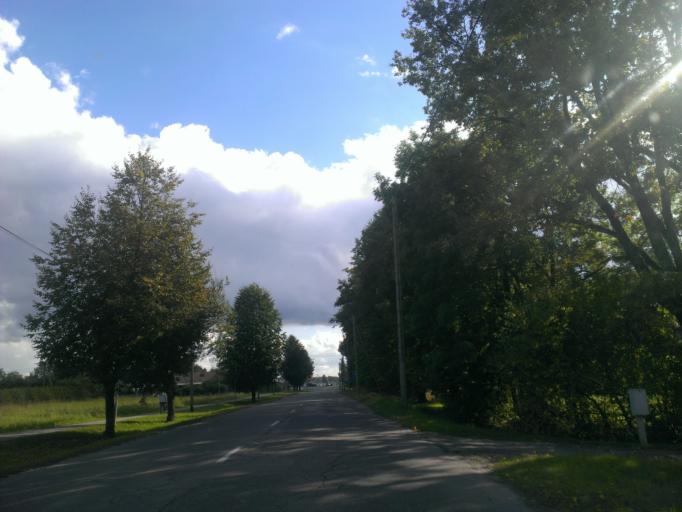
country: LV
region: Sigulda
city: Sigulda
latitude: 57.1475
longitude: 24.8569
